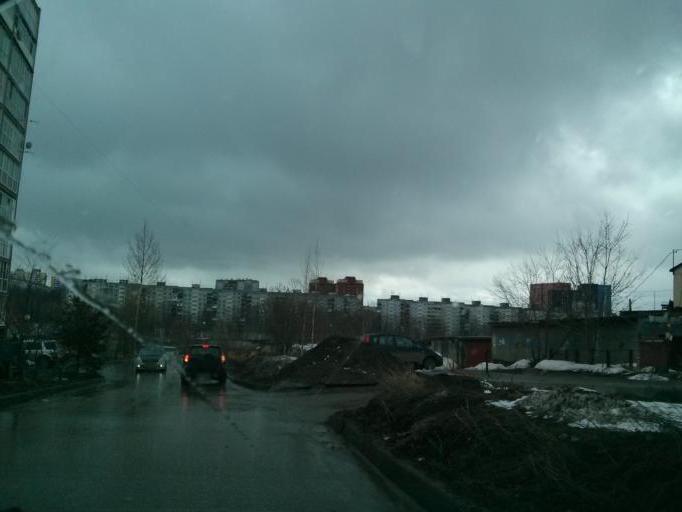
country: RU
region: Nizjnij Novgorod
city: Afonino
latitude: 56.3029
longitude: 44.0662
